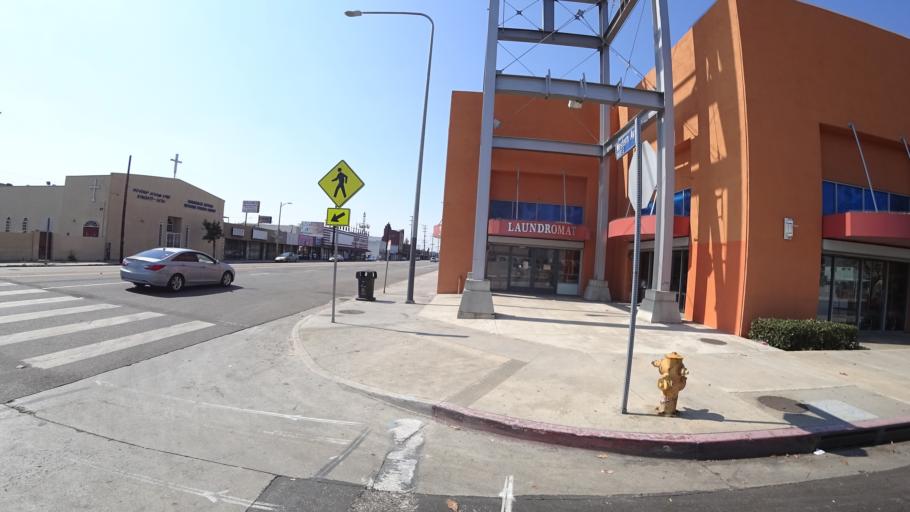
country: US
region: California
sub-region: Los Angeles County
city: Westmont
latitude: 33.9581
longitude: -118.3092
